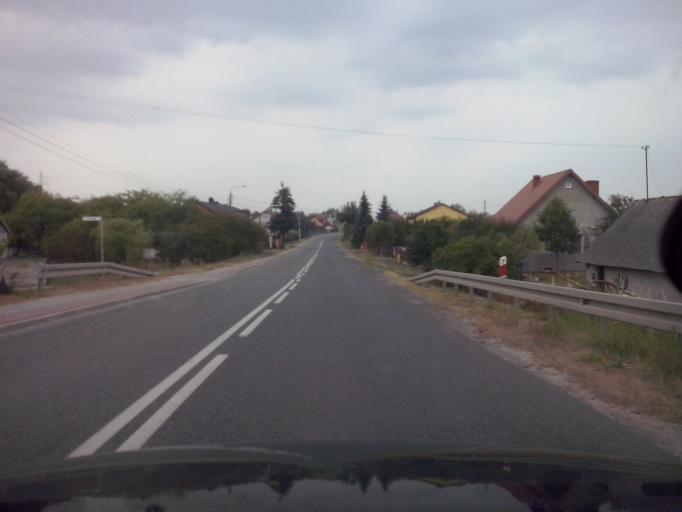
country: PL
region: Swietokrzyskie
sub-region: Powiat kielecki
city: Brzeziny
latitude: 50.7752
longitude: 20.5668
